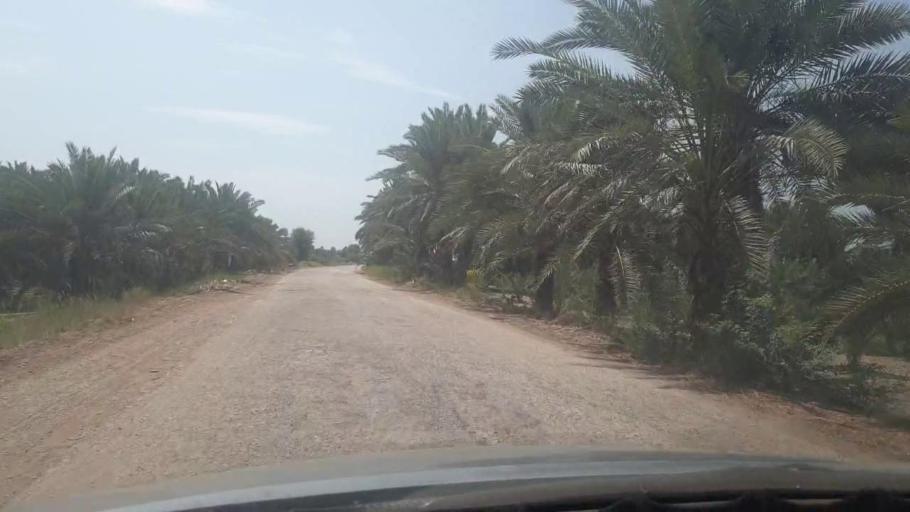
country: PK
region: Sindh
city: Bozdar
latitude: 27.2020
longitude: 68.5829
